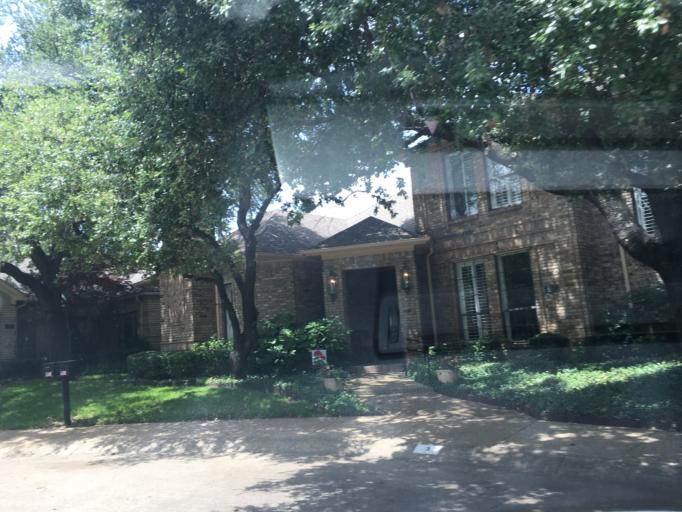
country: US
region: Texas
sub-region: Dallas County
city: University Park
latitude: 32.8720
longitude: -96.7826
